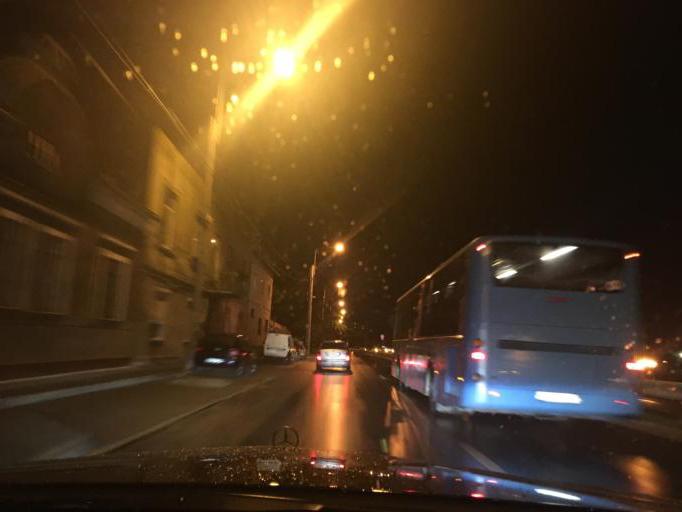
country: RO
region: Bihor
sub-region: Comuna Biharea
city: Oradea
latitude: 47.0525
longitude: 21.9495
